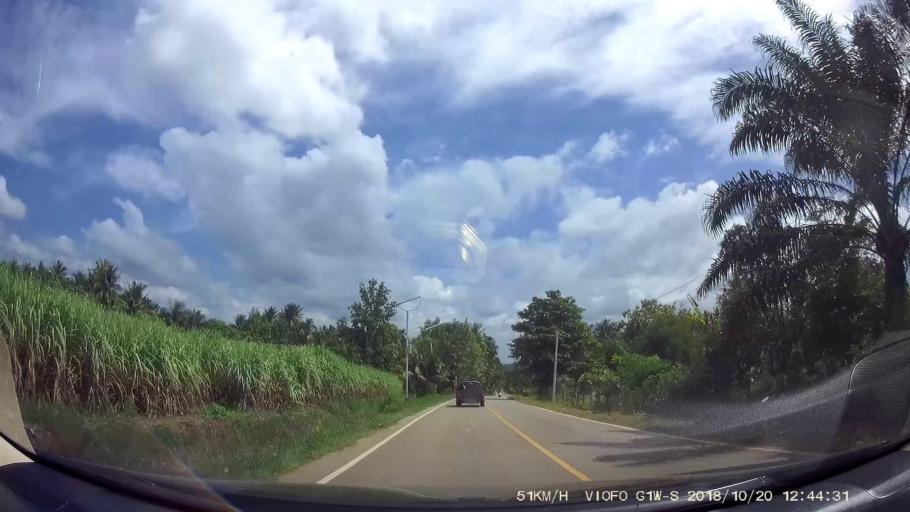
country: TH
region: Chaiyaphum
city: Khon San
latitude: 16.5387
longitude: 101.8696
